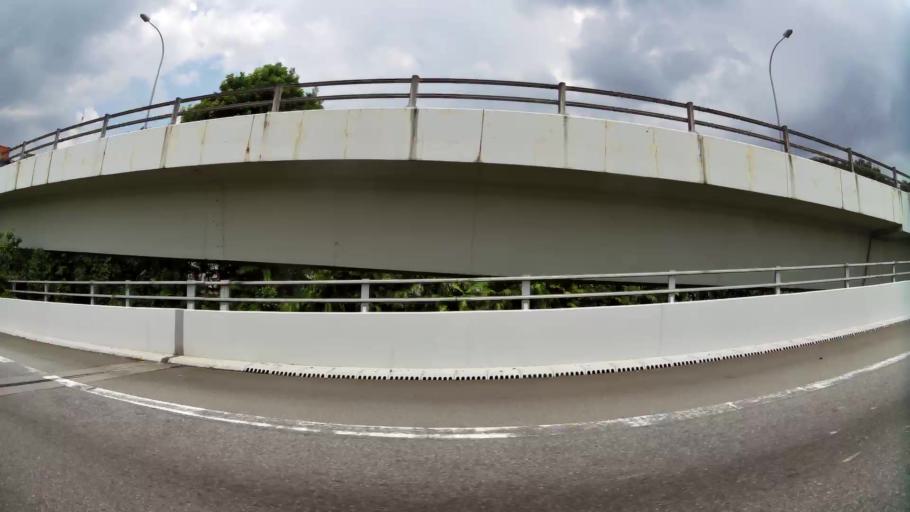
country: SG
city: Singapore
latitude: 1.2790
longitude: 103.7844
